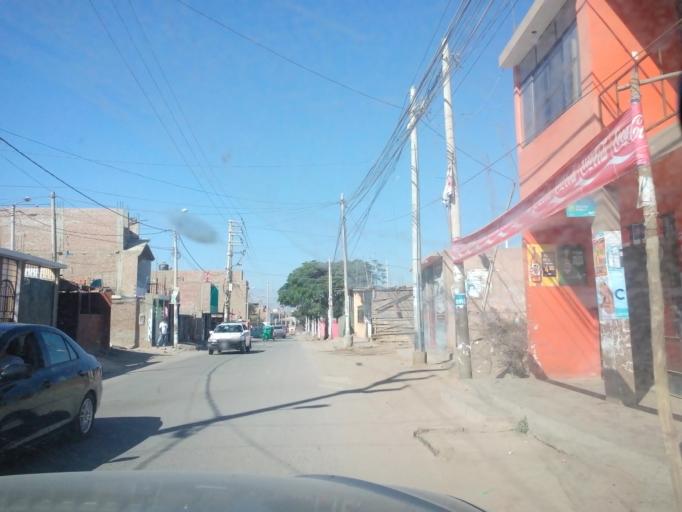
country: PE
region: Ica
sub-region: Provincia de Ica
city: Ica
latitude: -14.0737
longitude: -75.7492
